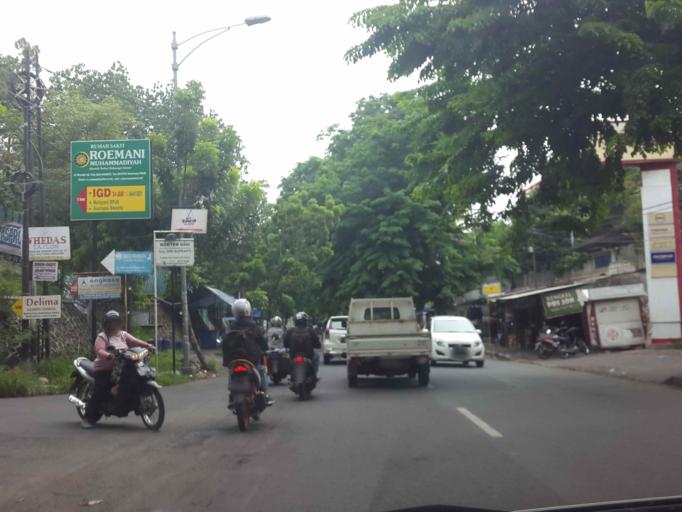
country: ID
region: Central Java
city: Semarang
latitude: -7.0036
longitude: 110.4261
